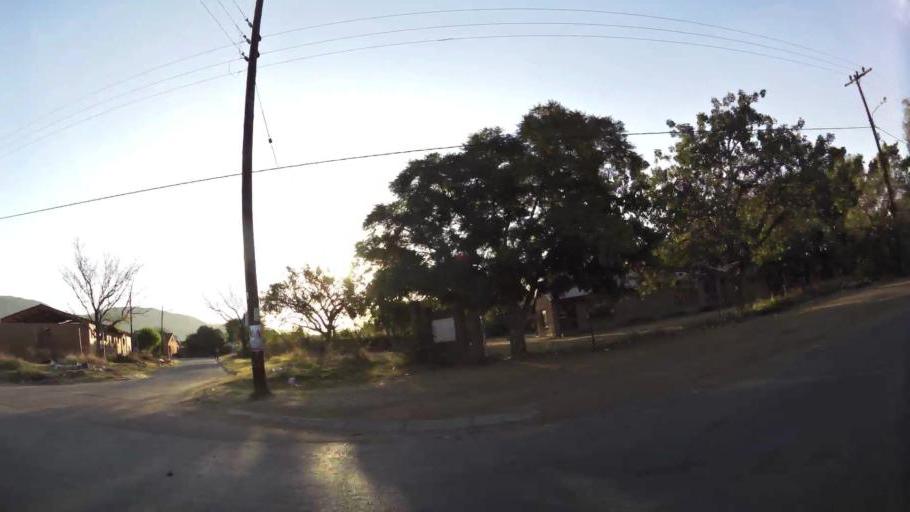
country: ZA
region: North-West
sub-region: Bojanala Platinum District Municipality
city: Rustenburg
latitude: -25.6415
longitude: 27.2106
